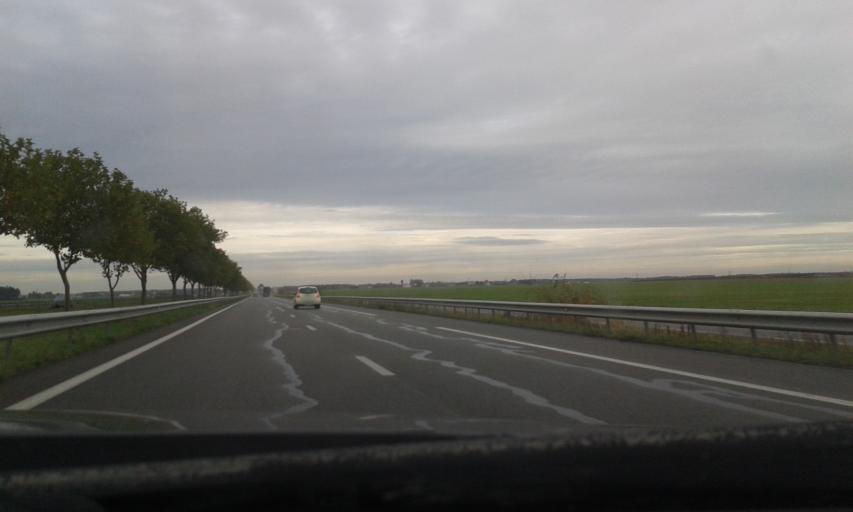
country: FR
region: Centre
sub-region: Departement d'Eure-et-Loir
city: Luray
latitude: 48.6584
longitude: 1.3952
